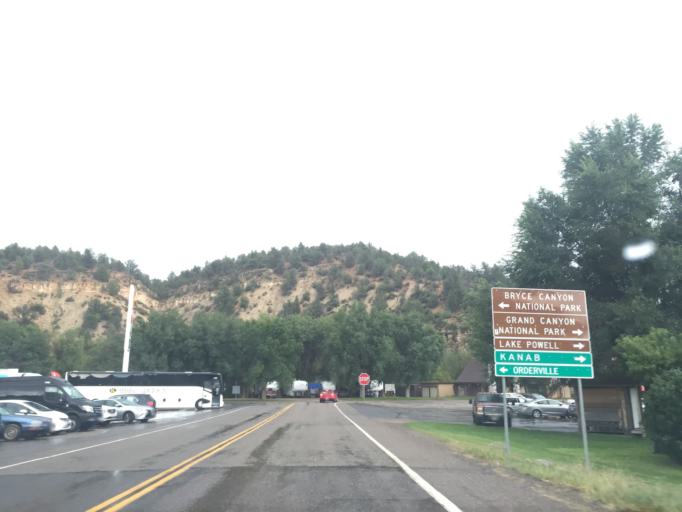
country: US
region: Utah
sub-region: Kane County
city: Kanab
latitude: 37.2237
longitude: -112.6818
